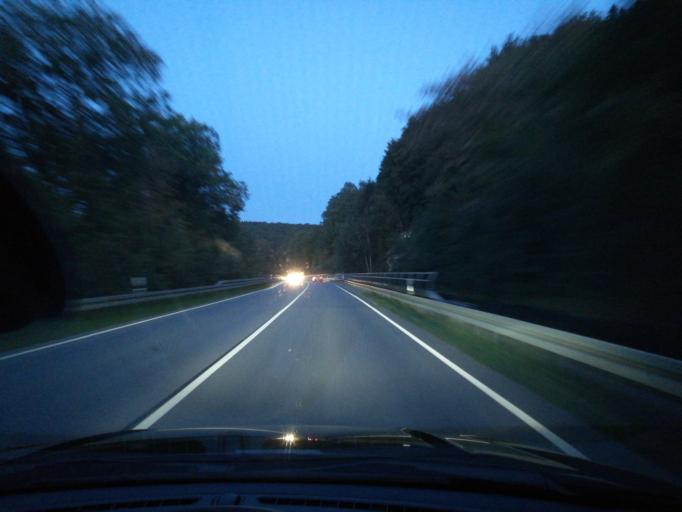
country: DE
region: Bavaria
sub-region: Lower Bavaria
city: Saal
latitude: 48.9037
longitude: 11.9521
